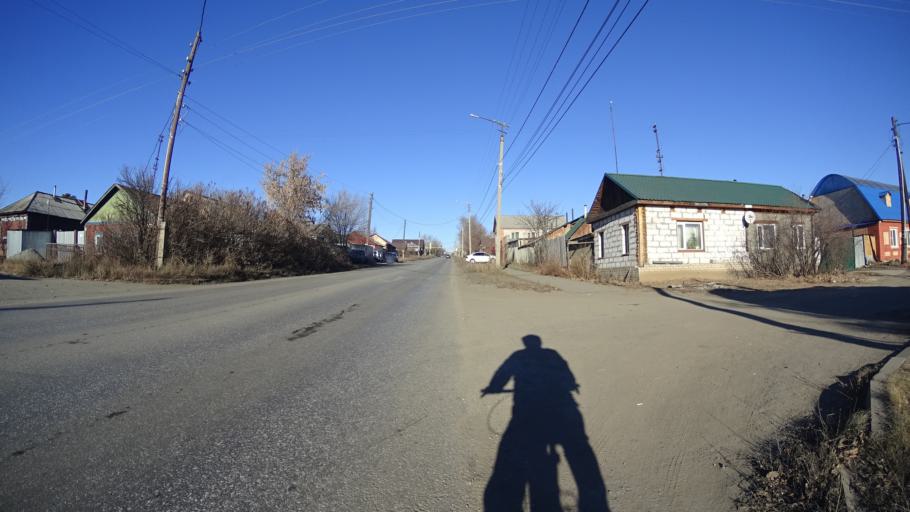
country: RU
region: Chelyabinsk
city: Troitsk
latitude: 54.0981
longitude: 61.5629
